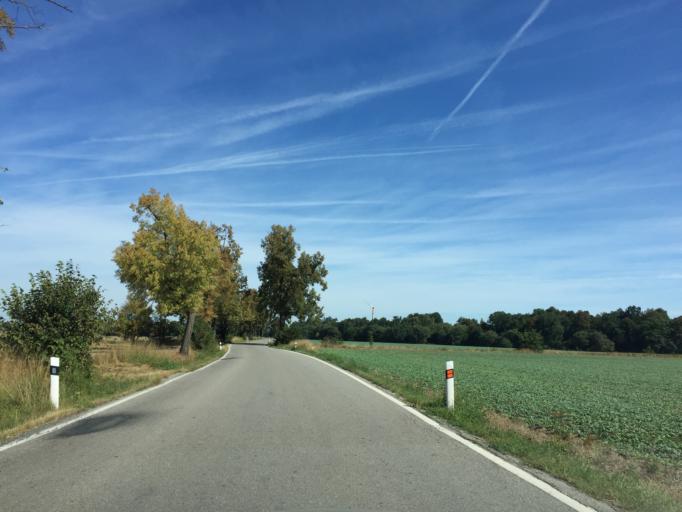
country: CZ
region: Jihocesky
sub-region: Okres Ceske Budejovice
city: Ceske Budejovice
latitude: 48.9477
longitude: 14.4825
